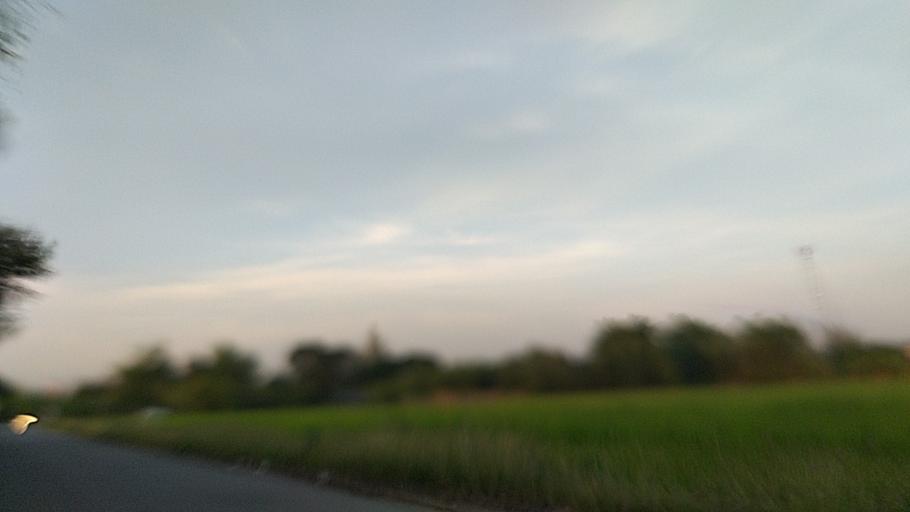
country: TH
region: Pathum Thani
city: Nong Suea
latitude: 14.0661
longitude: 100.8679
